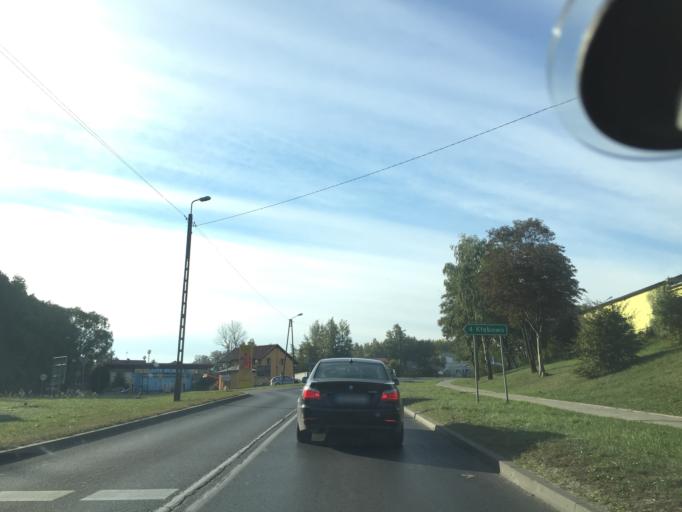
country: PL
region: Warmian-Masurian Voivodeship
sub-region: Powiat lidzbarski
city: Lidzbark Warminski
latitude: 54.1185
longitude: 20.5731
